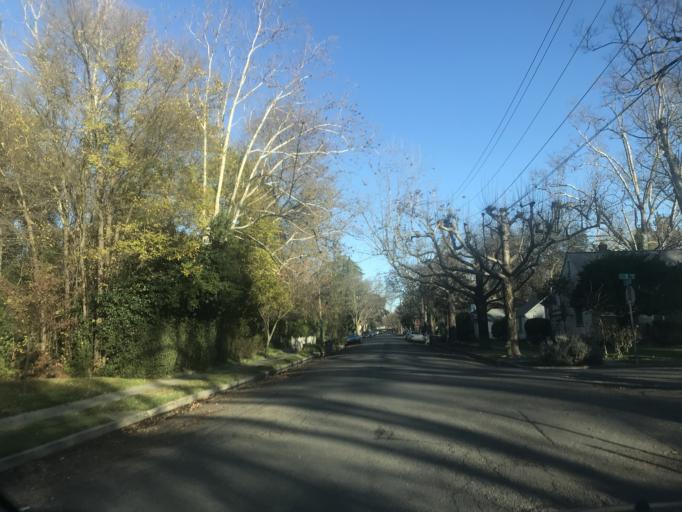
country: US
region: California
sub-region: Yolo County
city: Davis
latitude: 38.5495
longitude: -121.7454
